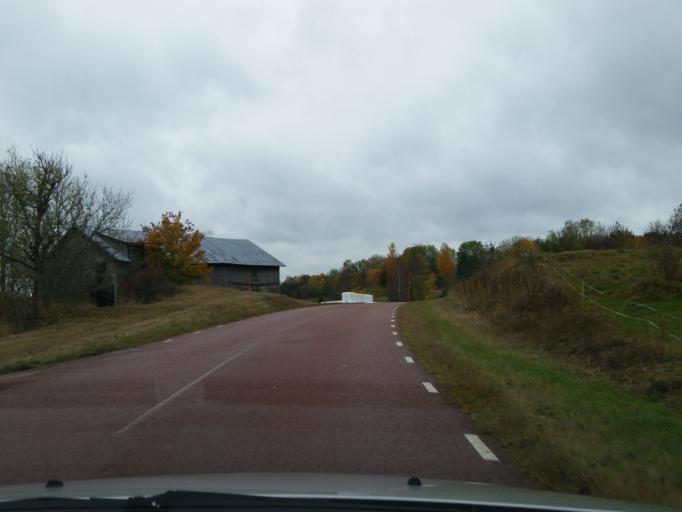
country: AX
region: Alands landsbygd
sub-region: Lumparland
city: Lumparland
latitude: 60.1435
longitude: 20.2709
